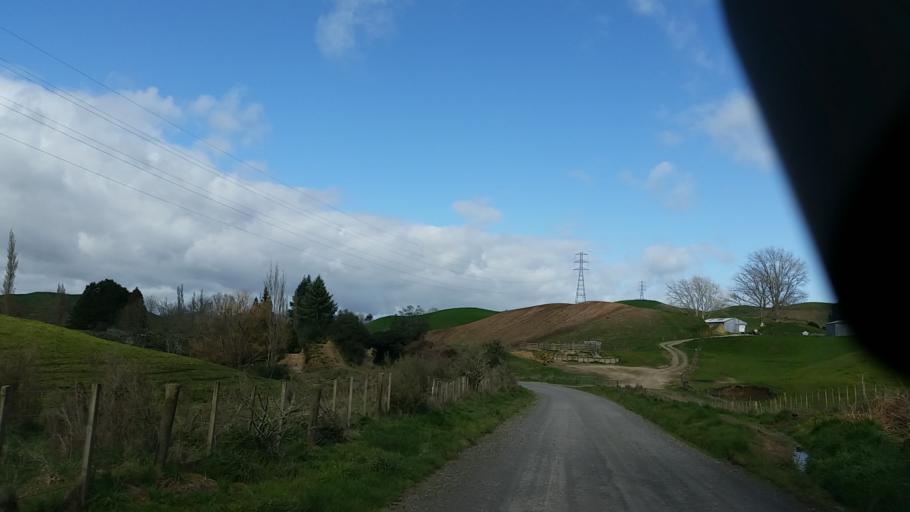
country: NZ
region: Waikato
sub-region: South Waikato District
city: Tokoroa
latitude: -38.3635
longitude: 176.0900
